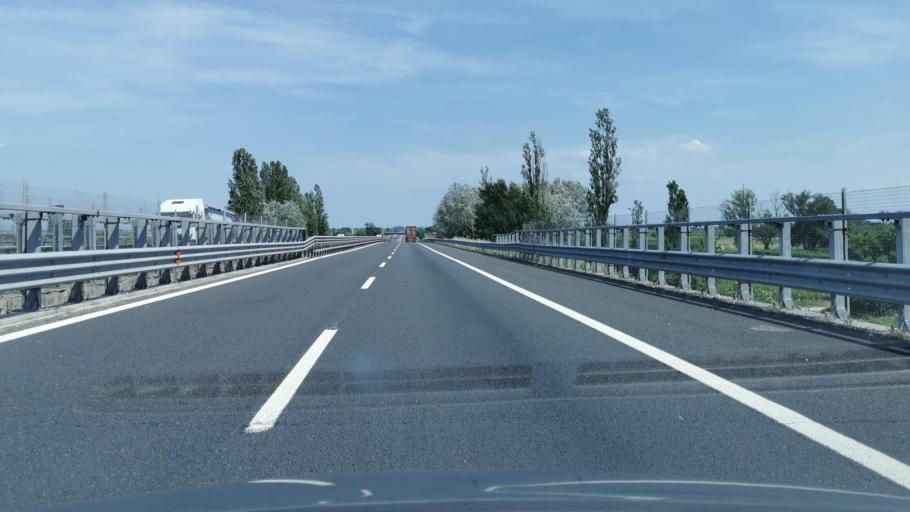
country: IT
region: Emilia-Romagna
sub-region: Provincia di Ravenna
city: Russi
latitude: 44.4060
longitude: 12.0254
